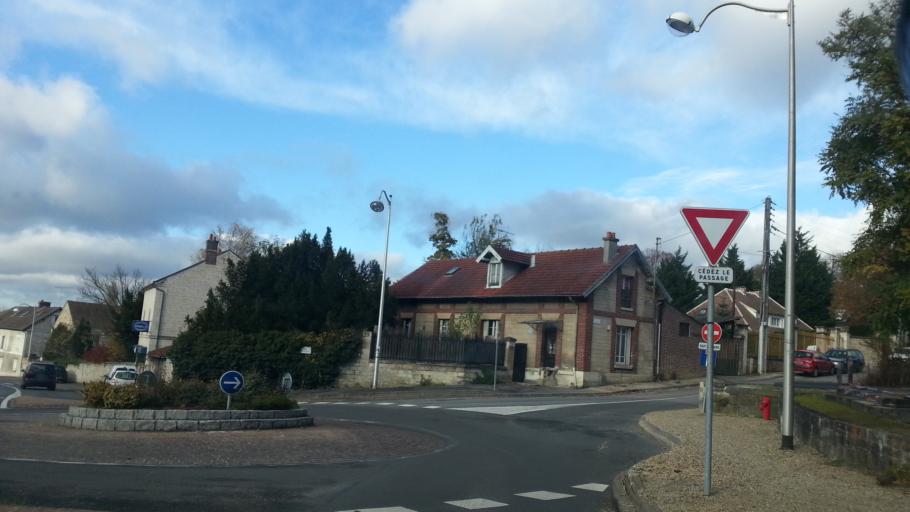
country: FR
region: Picardie
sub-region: Departement de l'Oise
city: Gouvieux
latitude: 49.1882
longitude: 2.4275
